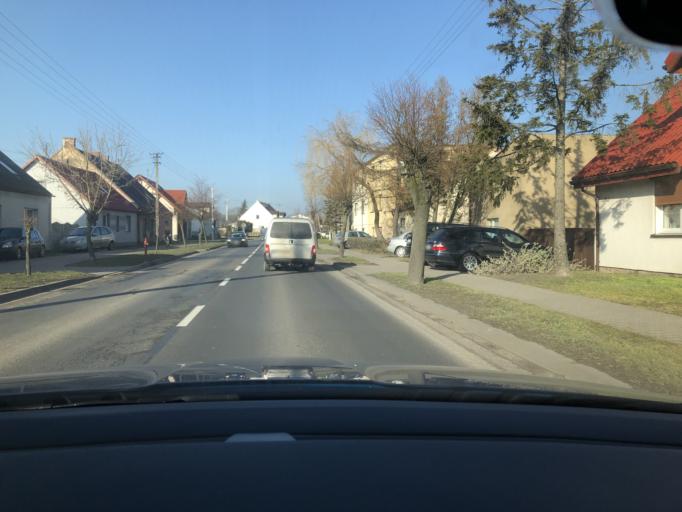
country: PL
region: Greater Poland Voivodeship
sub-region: Powiat szamotulski
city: Duszniki
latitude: 52.4444
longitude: 16.4075
